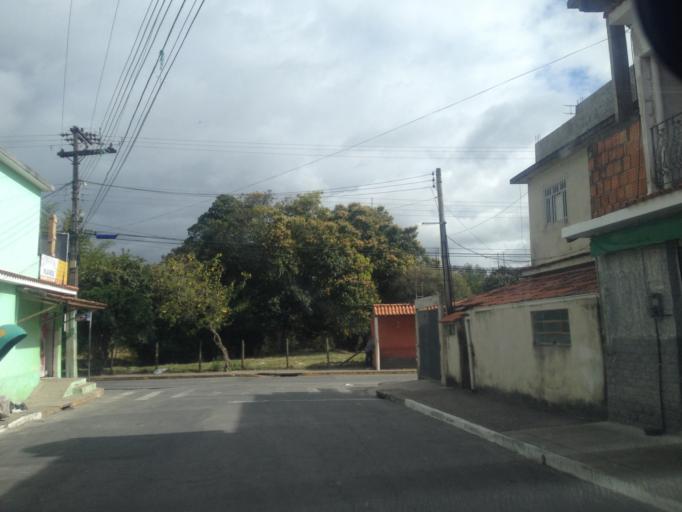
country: BR
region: Rio de Janeiro
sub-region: Porto Real
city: Porto Real
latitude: -22.4085
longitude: -44.3048
